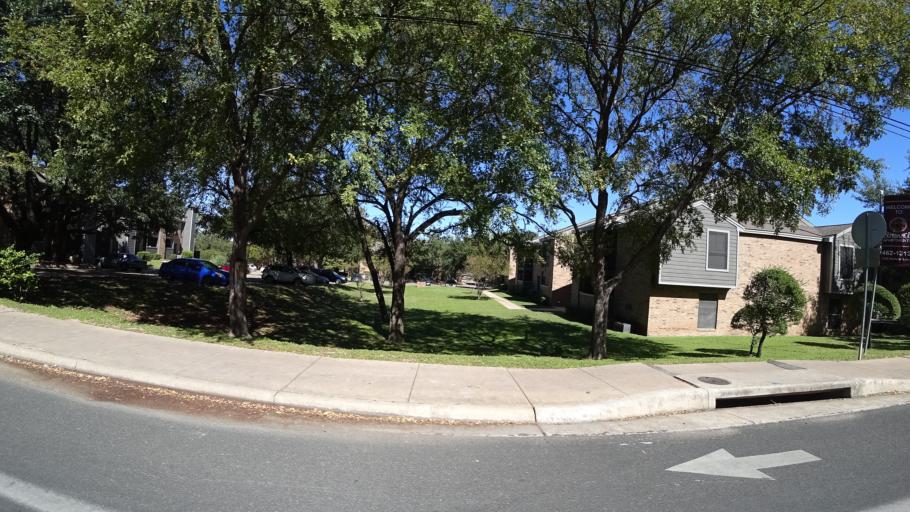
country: US
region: Texas
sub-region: Travis County
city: Austin
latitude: 30.2297
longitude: -97.7750
